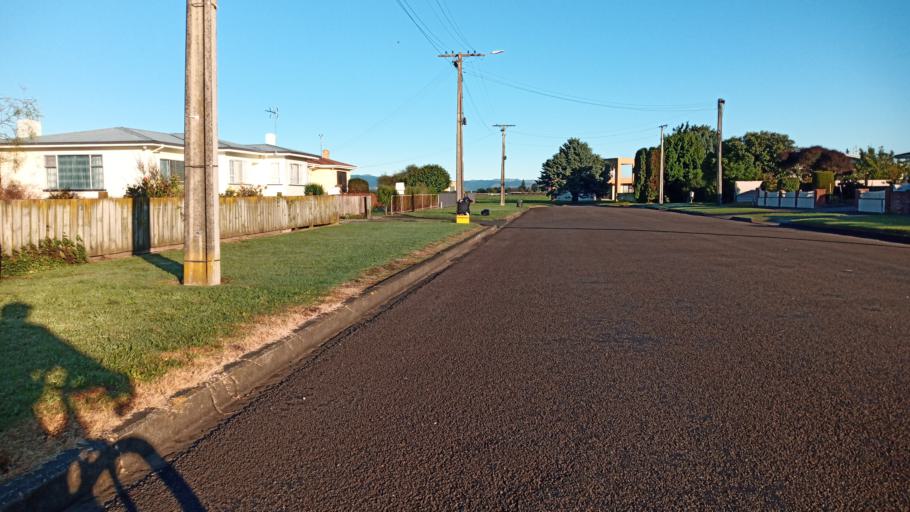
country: NZ
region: Gisborne
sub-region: Gisborne District
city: Gisborne
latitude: -38.6594
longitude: 177.9866
